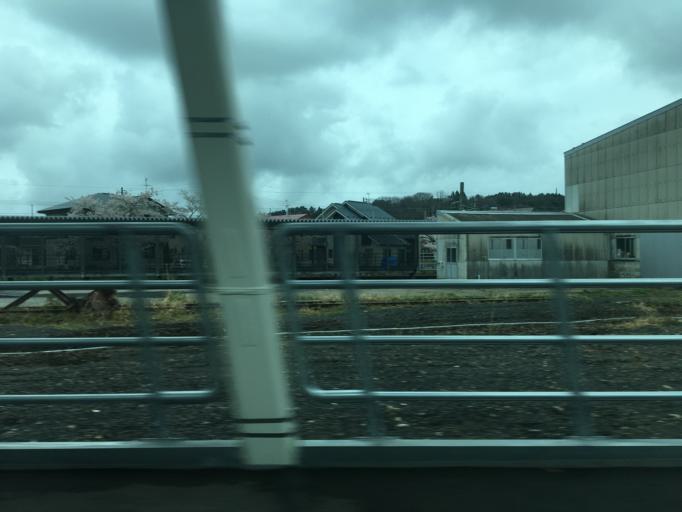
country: JP
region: Akita
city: Akita
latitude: 39.7379
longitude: 140.1125
